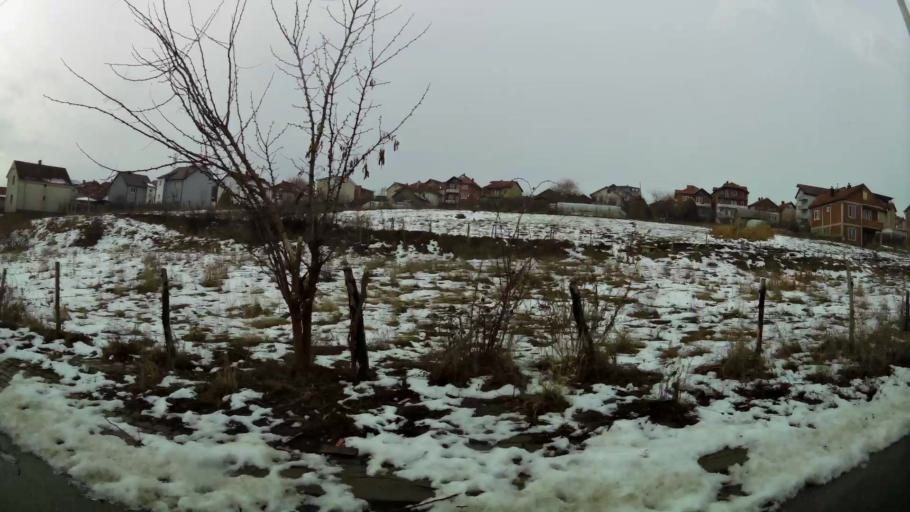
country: XK
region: Pristina
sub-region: Komuna e Prishtines
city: Pristina
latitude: 42.6866
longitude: 21.1627
